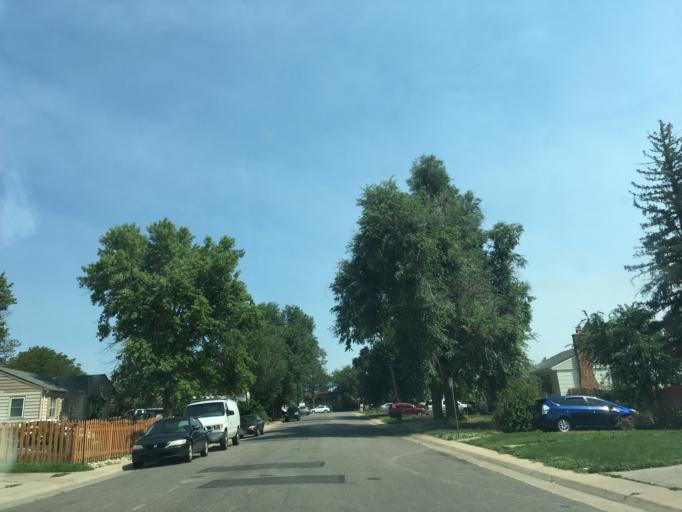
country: US
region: Colorado
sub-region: Jefferson County
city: Lakewood
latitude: 39.6954
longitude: -105.0448
